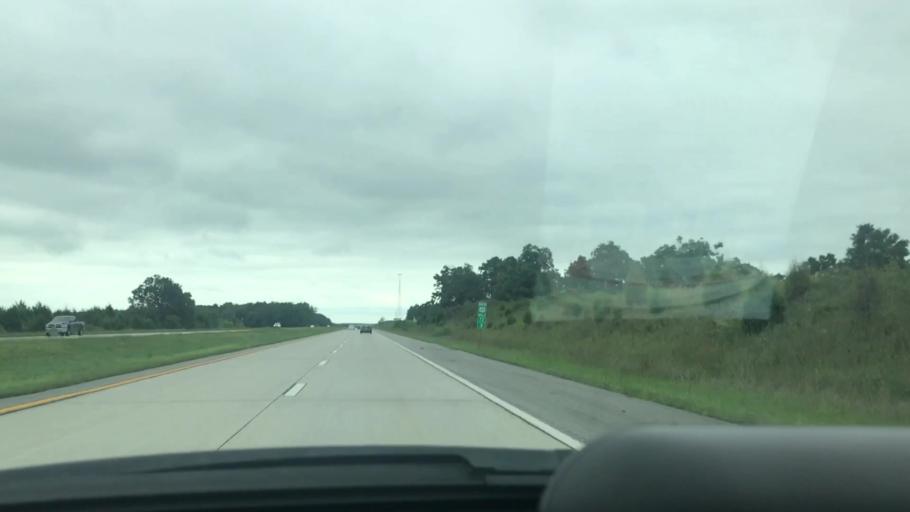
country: US
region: Missouri
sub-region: Greene County
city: Fair Grove
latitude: 37.4972
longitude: -93.1389
